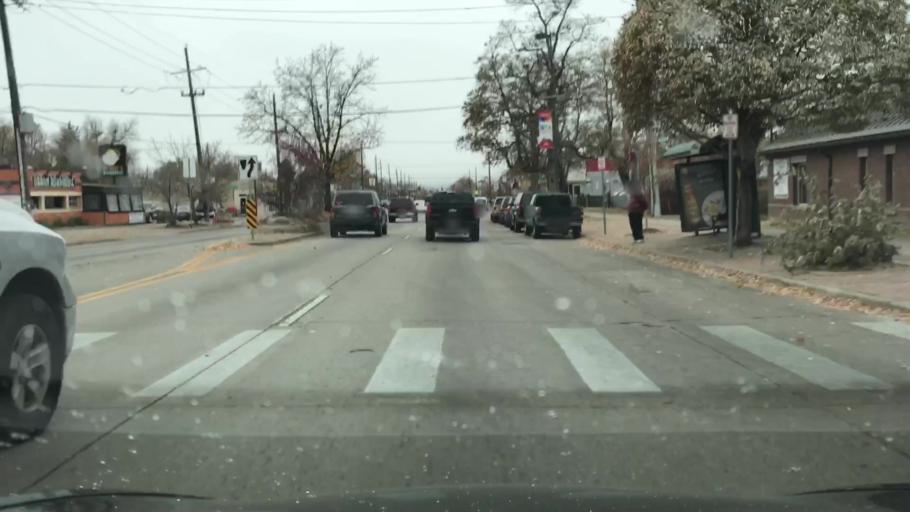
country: US
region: Colorado
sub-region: Arapahoe County
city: Cherry Hills Village
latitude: 39.6785
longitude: -104.9654
